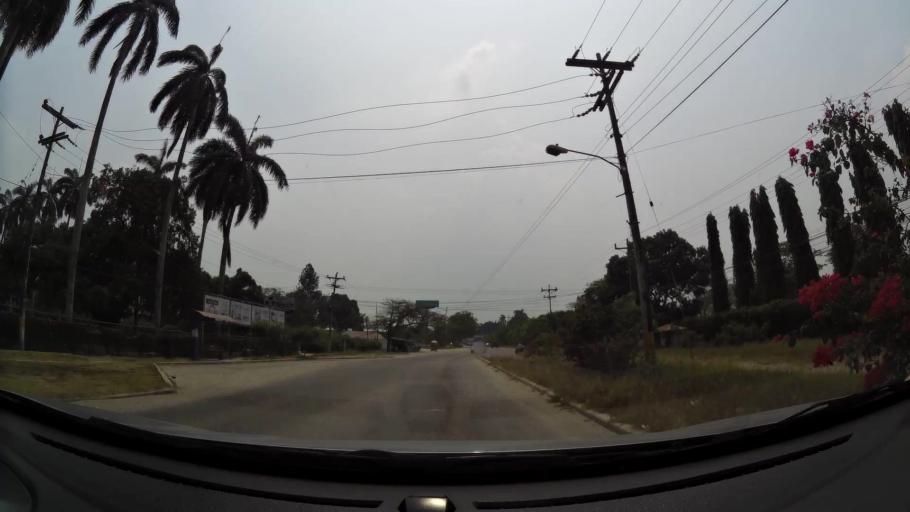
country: HN
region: Cortes
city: La Lima
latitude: 15.4366
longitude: -87.9191
